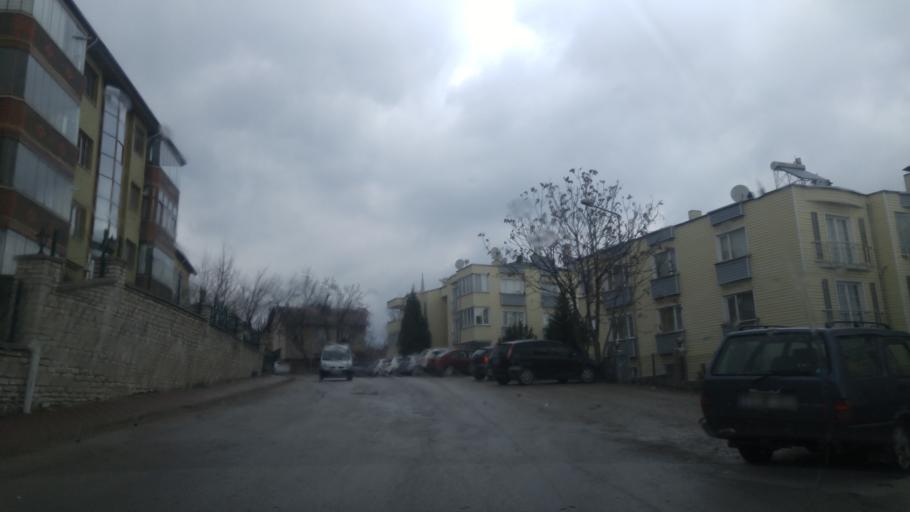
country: TR
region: Karabuk
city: Safranbolu
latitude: 41.2618
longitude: 32.6812
